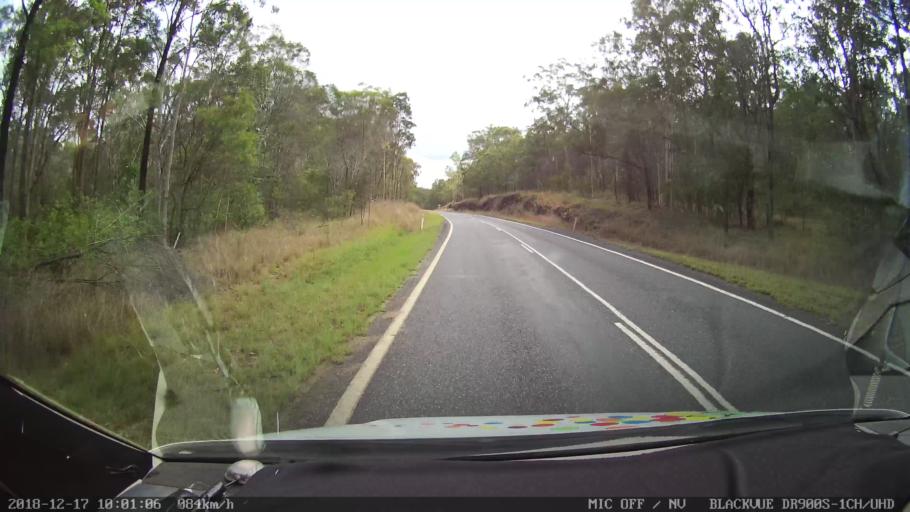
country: AU
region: New South Wales
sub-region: Tenterfield Municipality
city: Carrolls Creek
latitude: -28.9077
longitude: 152.4349
